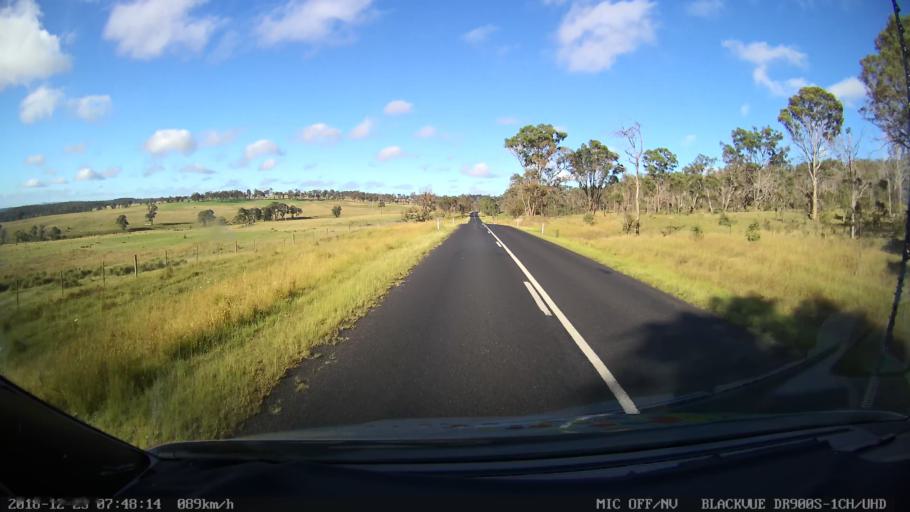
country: AU
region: New South Wales
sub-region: Armidale Dumaresq
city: Armidale
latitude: -30.5309
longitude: 151.8888
